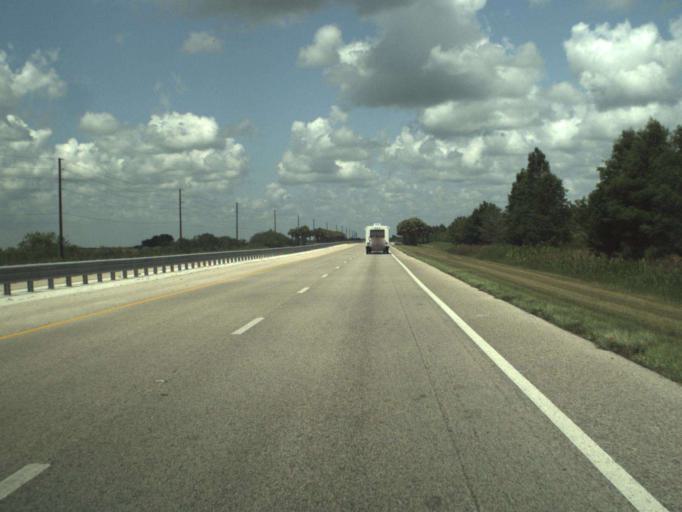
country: US
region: Florida
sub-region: Indian River County
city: Fellsmere
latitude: 27.6417
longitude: -80.7402
